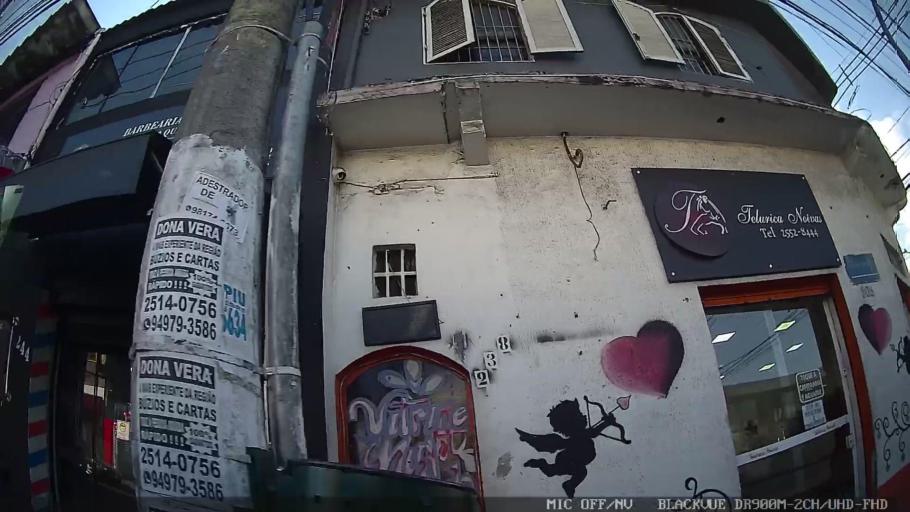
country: BR
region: Sao Paulo
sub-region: Ferraz De Vasconcelos
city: Ferraz de Vasconcelos
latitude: -23.5460
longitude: -46.4115
